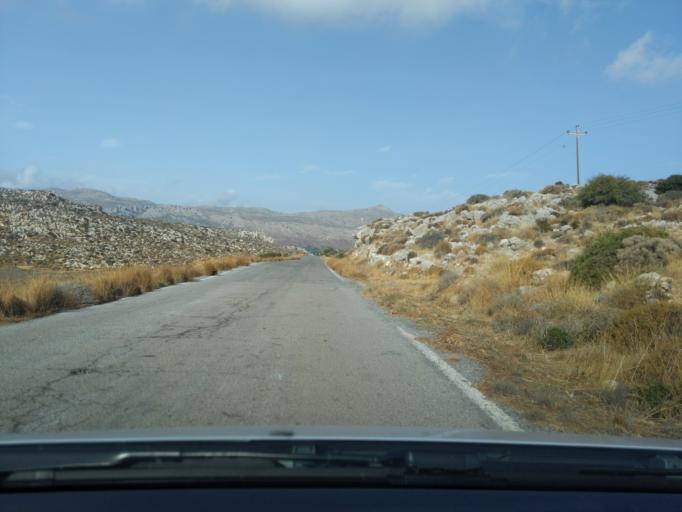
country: GR
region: Crete
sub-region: Nomos Lasithiou
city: Palekastro
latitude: 35.0849
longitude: 26.2546
